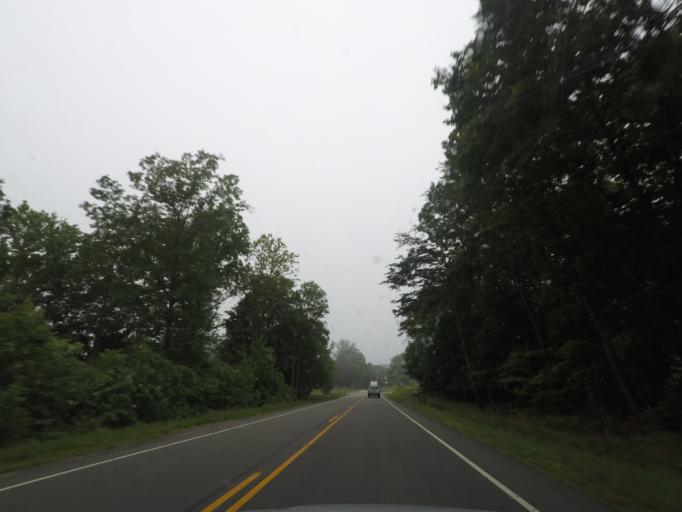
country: US
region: Virginia
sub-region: Buckingham County
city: Buckingham
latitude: 37.4579
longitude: -78.4643
